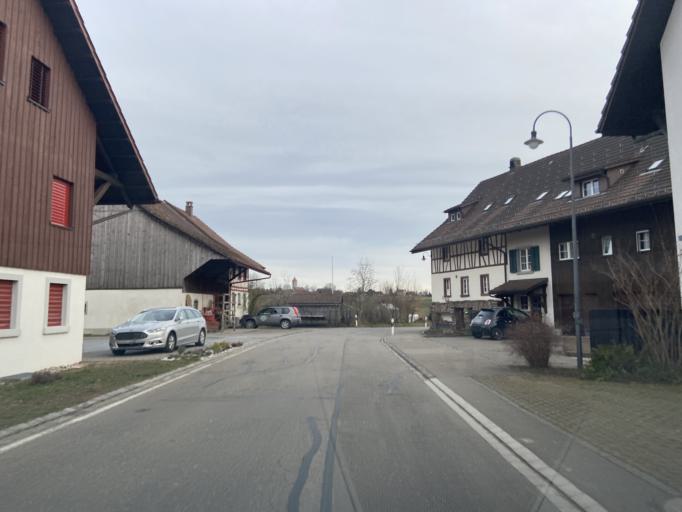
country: CH
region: Zurich
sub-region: Bezirk Winterthur
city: Brutten
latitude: 47.4786
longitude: 8.6646
